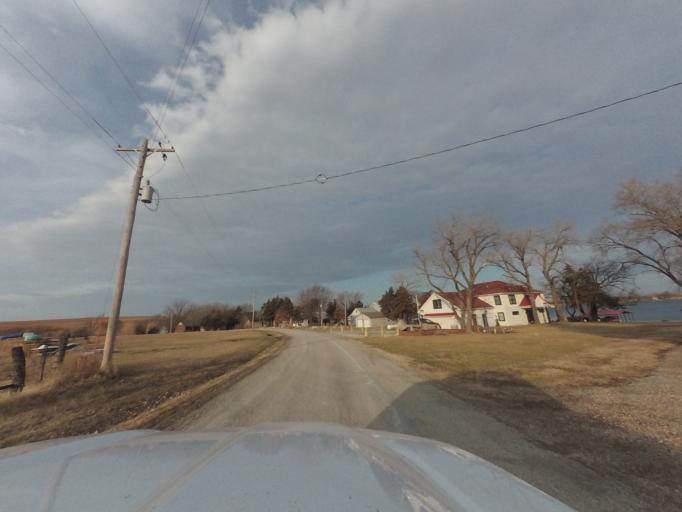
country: US
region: Kansas
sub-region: Morris County
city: Council Grove
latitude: 38.5180
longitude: -96.4125
